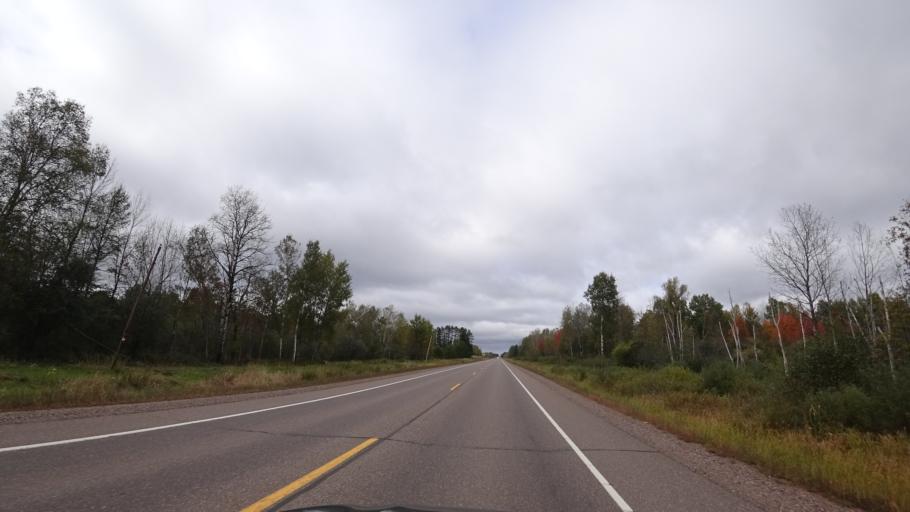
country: US
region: Wisconsin
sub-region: Rusk County
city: Ladysmith
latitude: 45.4878
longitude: -91.1115
